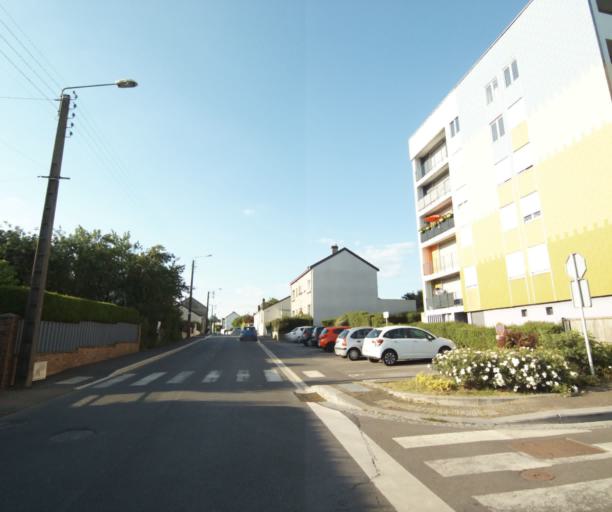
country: FR
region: Champagne-Ardenne
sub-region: Departement des Ardennes
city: Charleville-Mezieres
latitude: 49.7862
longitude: 4.7098
